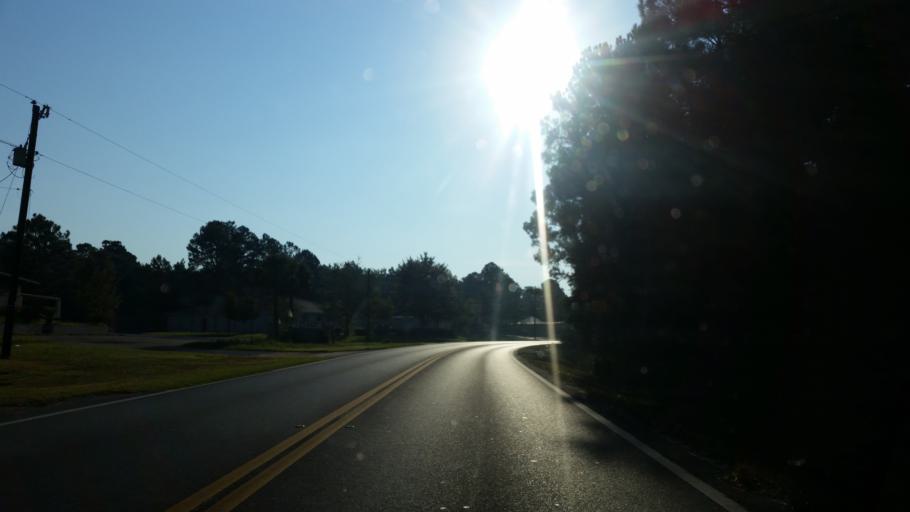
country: US
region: Florida
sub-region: Santa Rosa County
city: Milton
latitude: 30.6146
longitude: -87.0612
